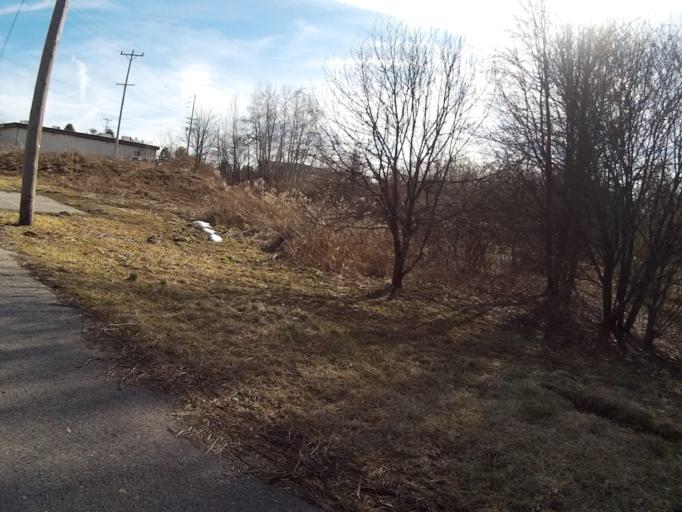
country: US
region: Pennsylvania
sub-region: Centre County
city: State College
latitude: 40.7851
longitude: -77.8756
